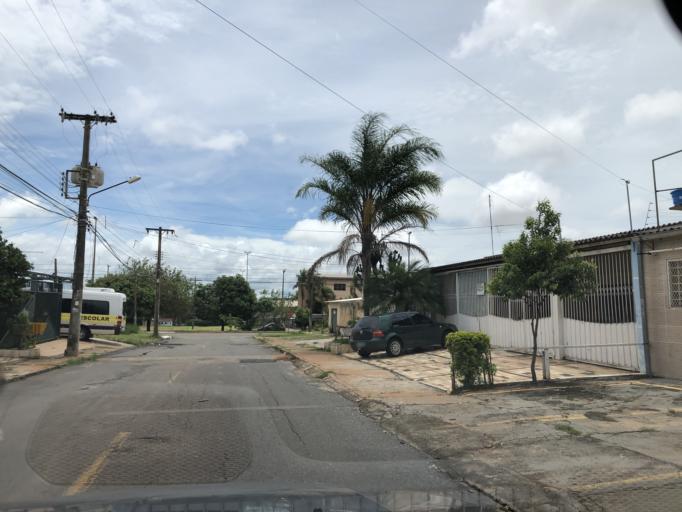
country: BR
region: Federal District
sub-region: Brasilia
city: Brasilia
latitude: -15.8089
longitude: -48.1024
